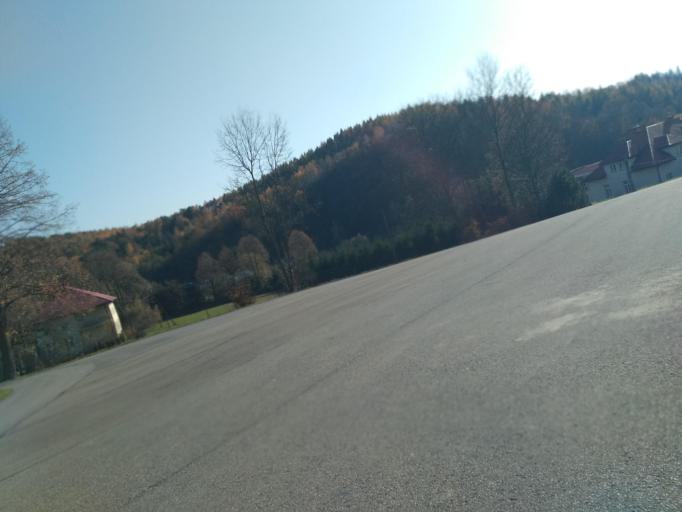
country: PL
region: Subcarpathian Voivodeship
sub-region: Powiat brzozowski
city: Nozdrzec
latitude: 49.8121
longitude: 22.1684
